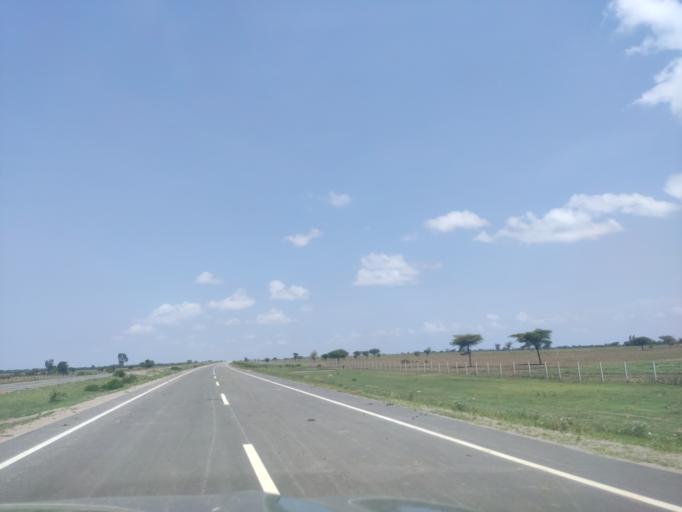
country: ET
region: Oromiya
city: Ziway
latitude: 8.2303
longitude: 38.8726
